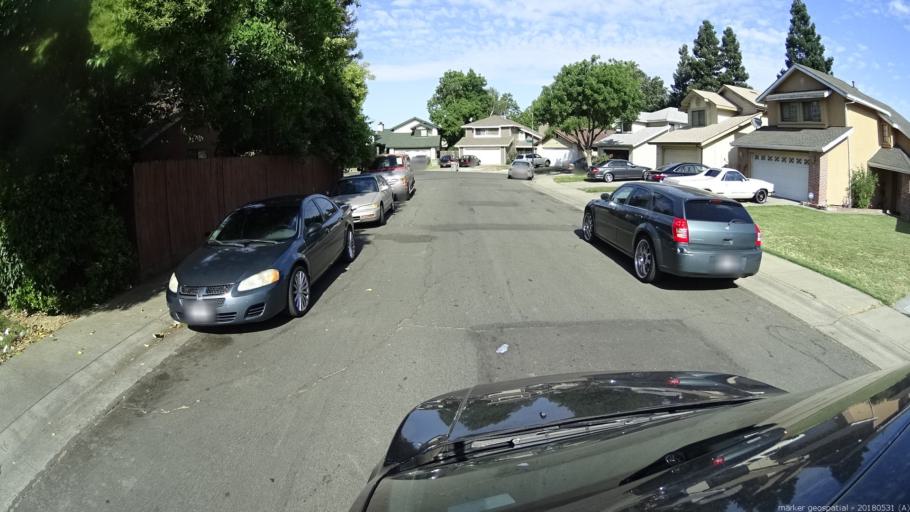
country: US
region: California
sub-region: Sacramento County
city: Sacramento
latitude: 38.6342
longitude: -121.4895
